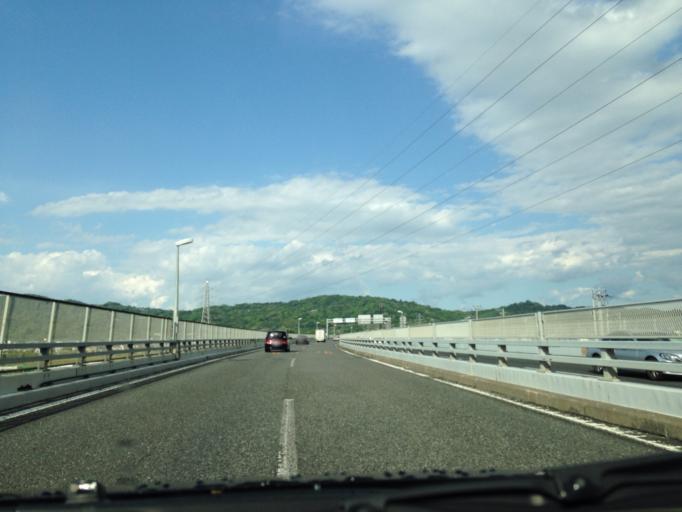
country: JP
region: Kanagawa
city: Odawara
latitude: 35.2896
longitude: 139.1765
